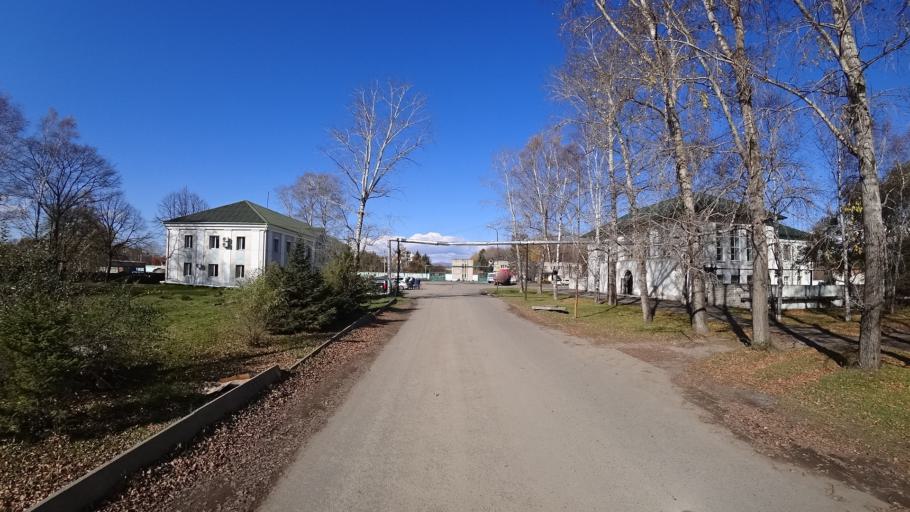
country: RU
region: Khabarovsk Krai
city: Amursk
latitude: 50.0997
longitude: 136.4904
